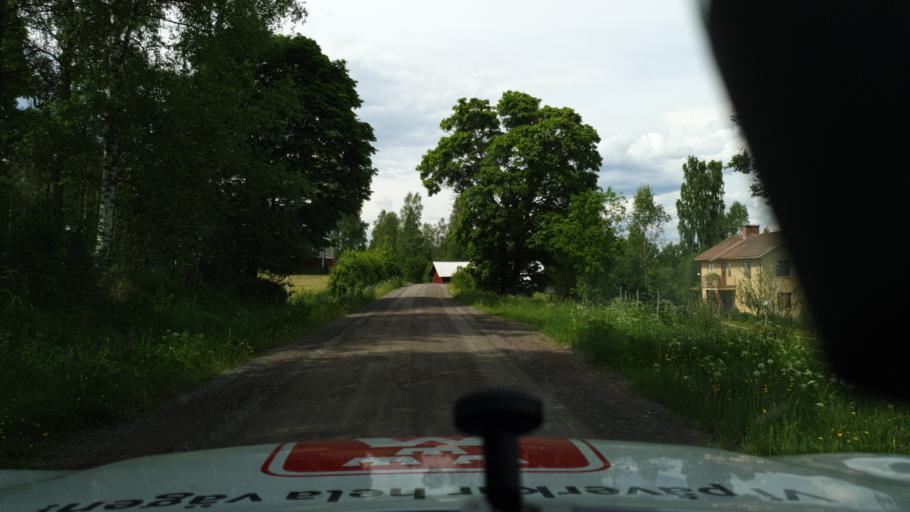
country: SE
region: Vaermland
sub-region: Torsby Kommun
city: Torsby
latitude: 59.9752
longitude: 12.8555
